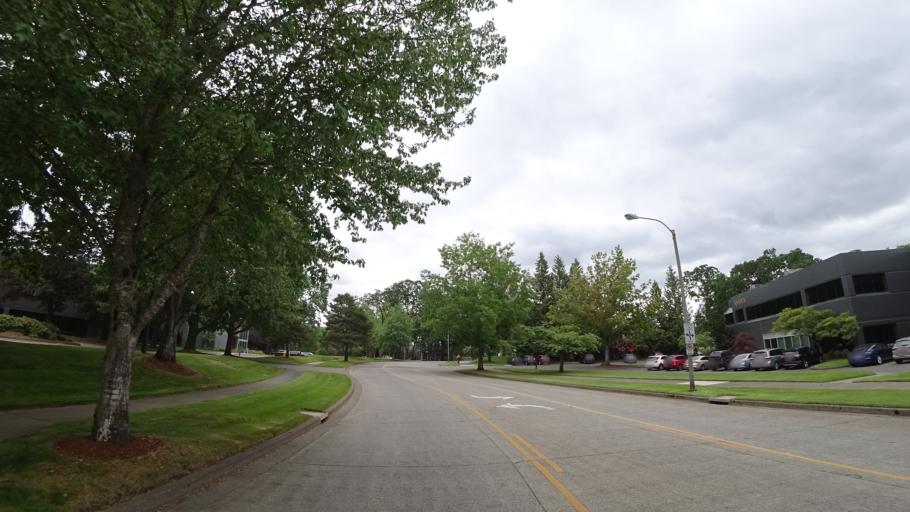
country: US
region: Oregon
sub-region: Washington County
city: Beaverton
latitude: 45.4597
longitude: -122.7931
